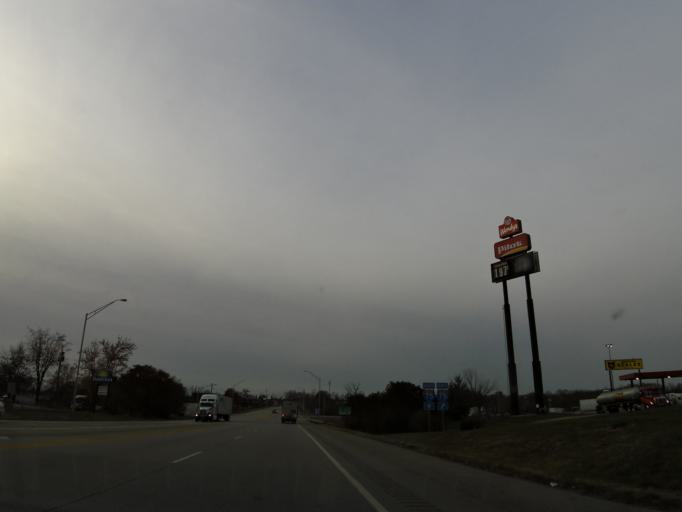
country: US
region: Kentucky
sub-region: Scott County
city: Georgetown
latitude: 38.2752
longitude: -84.5539
